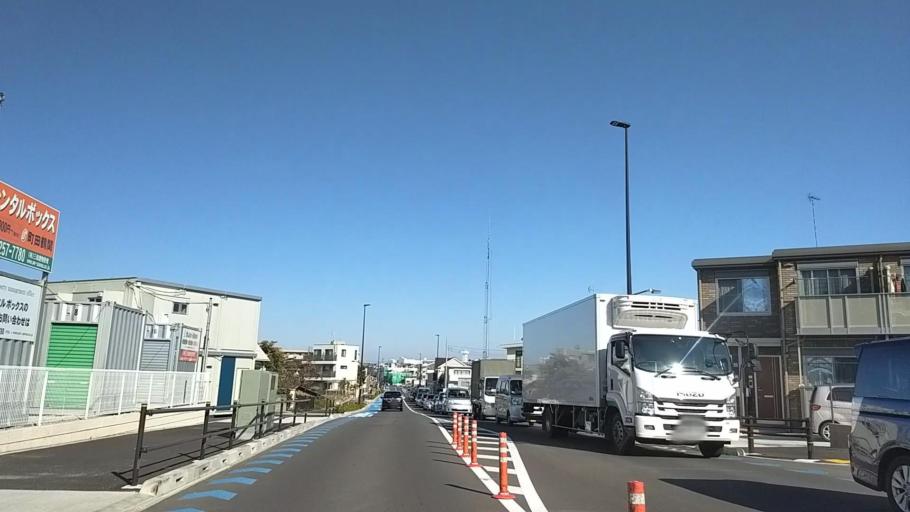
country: JP
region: Tokyo
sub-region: Machida-shi
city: Machida
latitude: 35.5142
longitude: 139.4652
